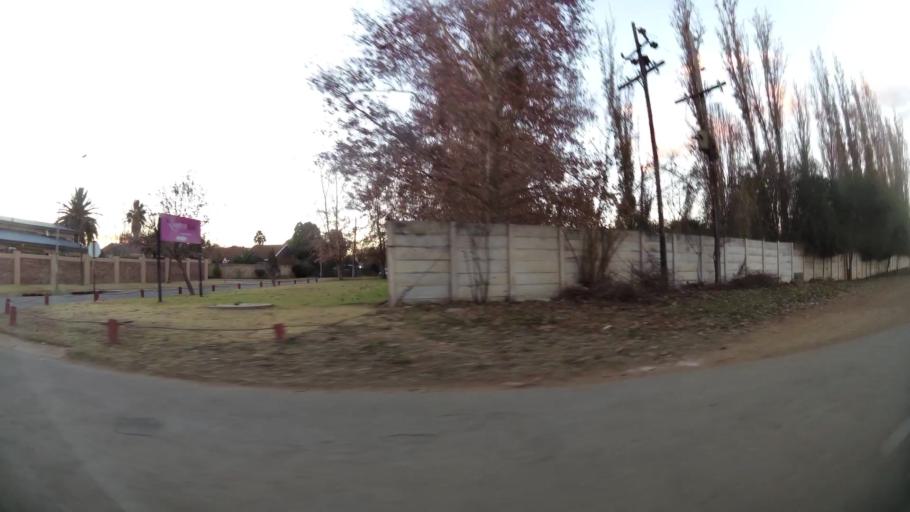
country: ZA
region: North-West
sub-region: Dr Kenneth Kaunda District Municipality
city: Potchefstroom
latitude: -26.7224
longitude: 27.1230
